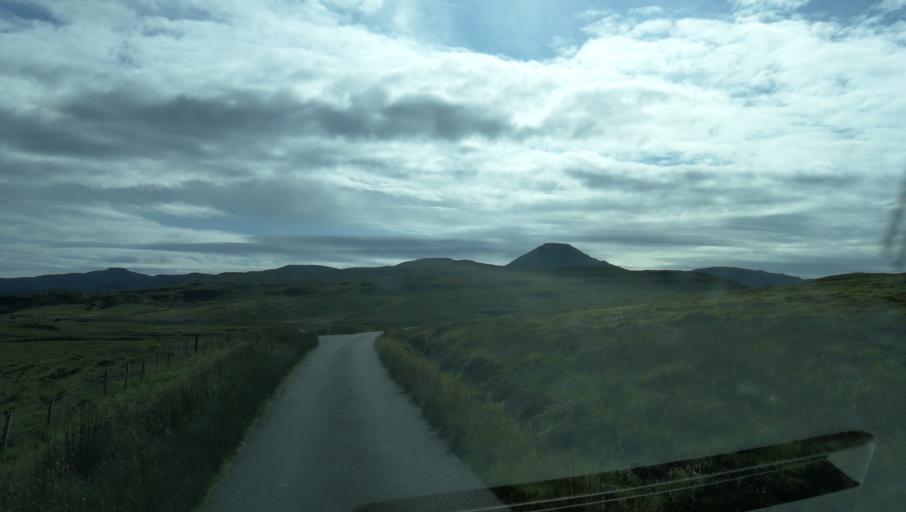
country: GB
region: Scotland
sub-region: Highland
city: Isle of Skye
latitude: 57.4096
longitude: -6.5658
